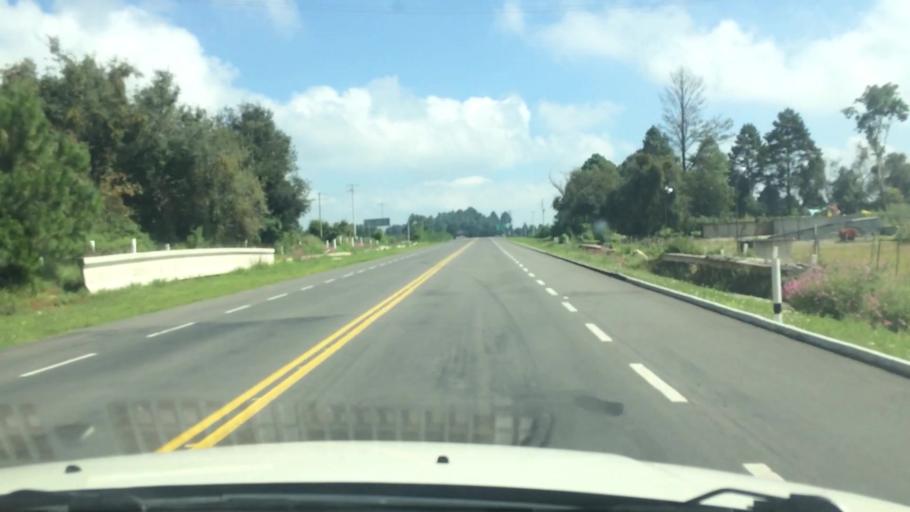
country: MX
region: Mexico
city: Amanalco de Becerra
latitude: 19.3389
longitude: -99.9942
